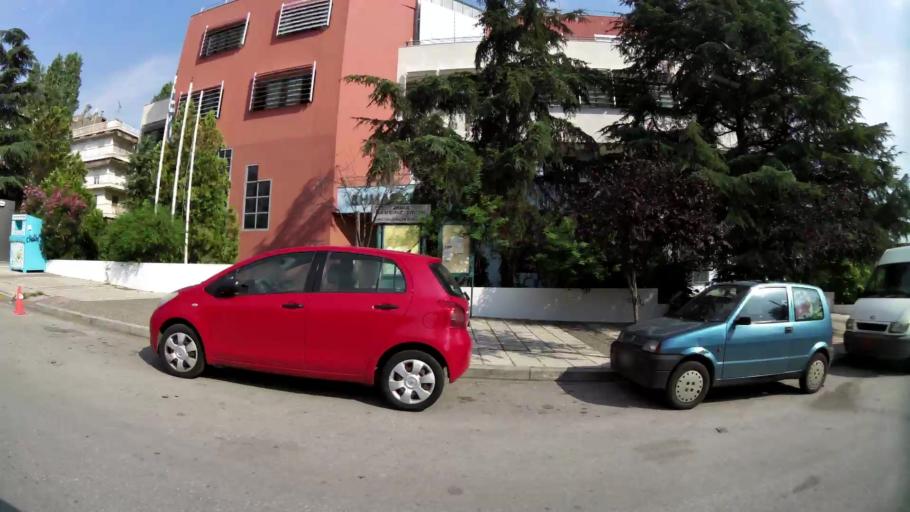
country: GR
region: Central Macedonia
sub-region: Nomos Thessalonikis
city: Sykies
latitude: 40.6540
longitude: 22.9443
